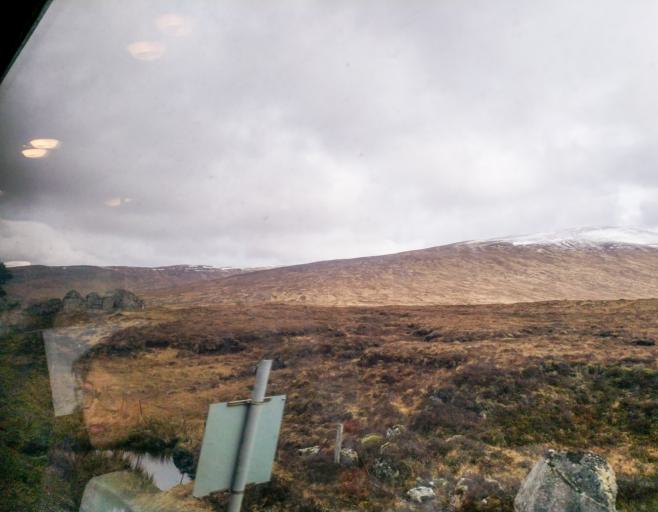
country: GB
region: Scotland
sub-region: Highland
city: Spean Bridge
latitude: 56.7587
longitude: -4.6884
